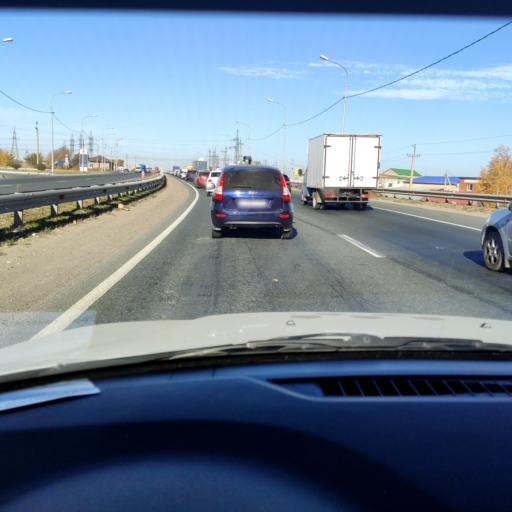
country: RU
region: Samara
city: Zhigulevsk
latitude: 53.5396
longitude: 49.5164
